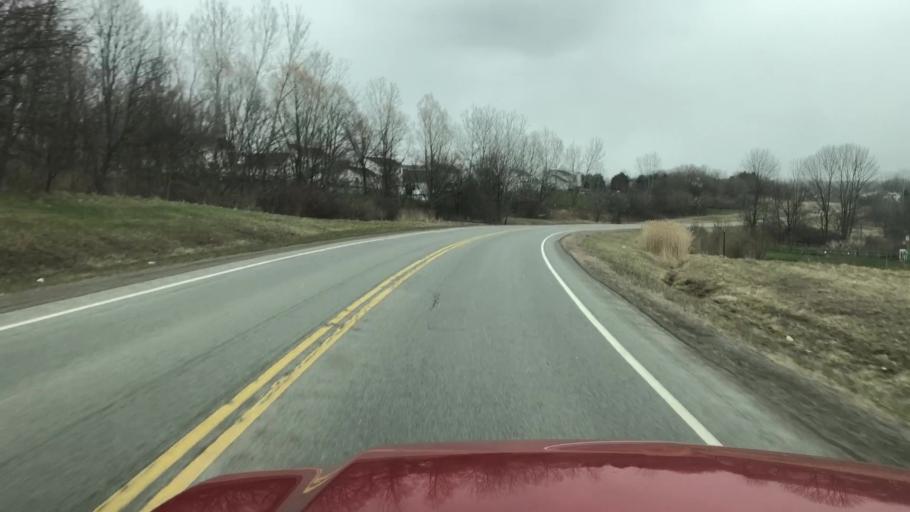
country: US
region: New York
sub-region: Monroe County
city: Fairport
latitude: 43.1307
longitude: -77.3609
